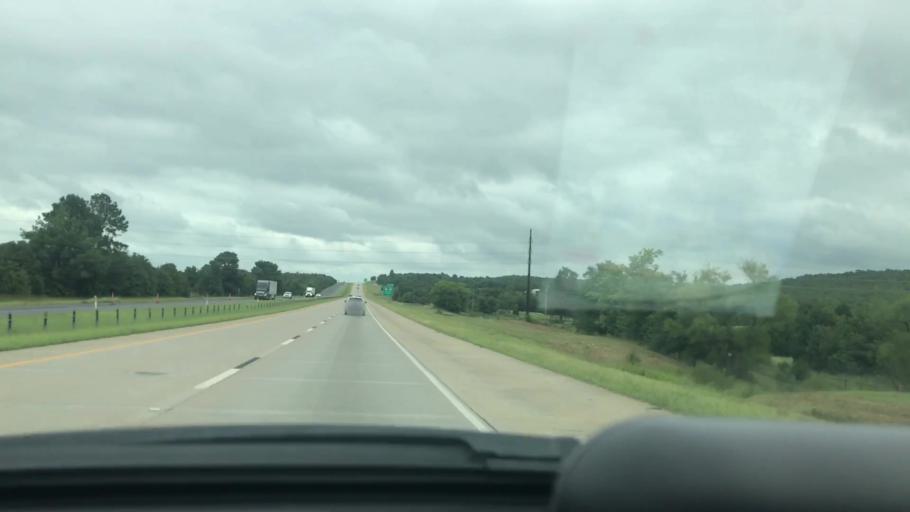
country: US
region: Oklahoma
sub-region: Pittsburg County
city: Krebs
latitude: 34.9759
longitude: -95.7231
